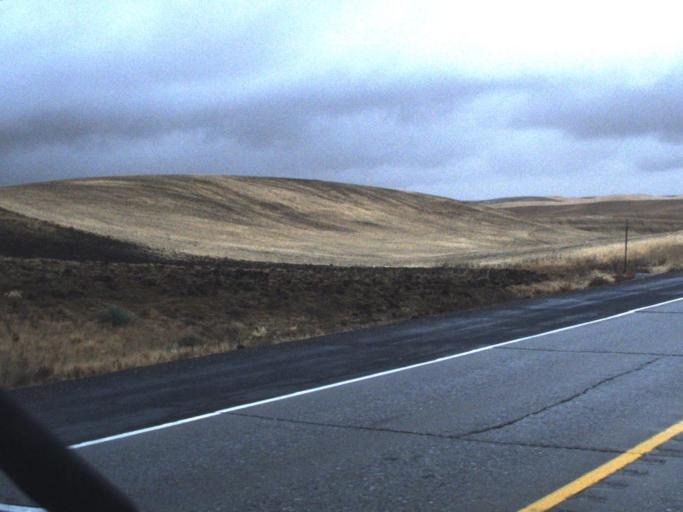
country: US
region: Washington
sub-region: Whitman County
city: Colfax
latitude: 47.1634
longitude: -117.3785
